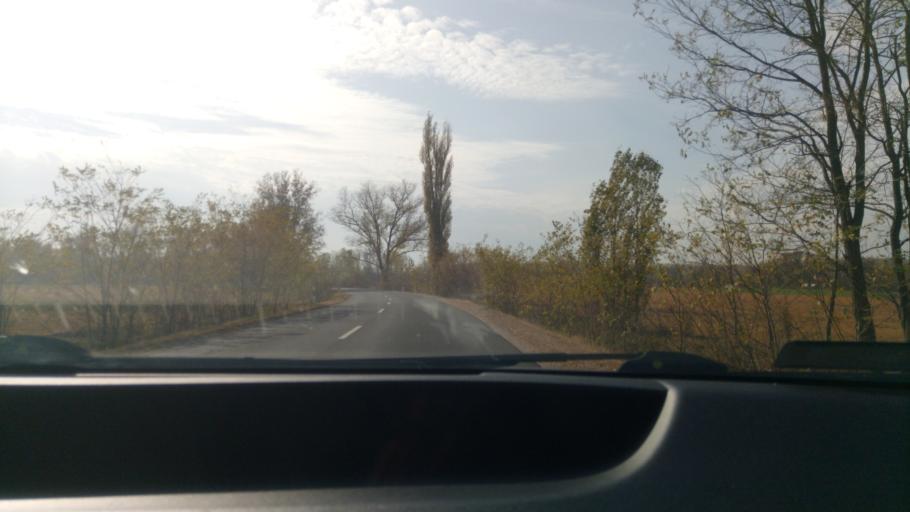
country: HU
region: Bacs-Kiskun
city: Jaszszentlaszlo
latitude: 46.5617
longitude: 19.7474
